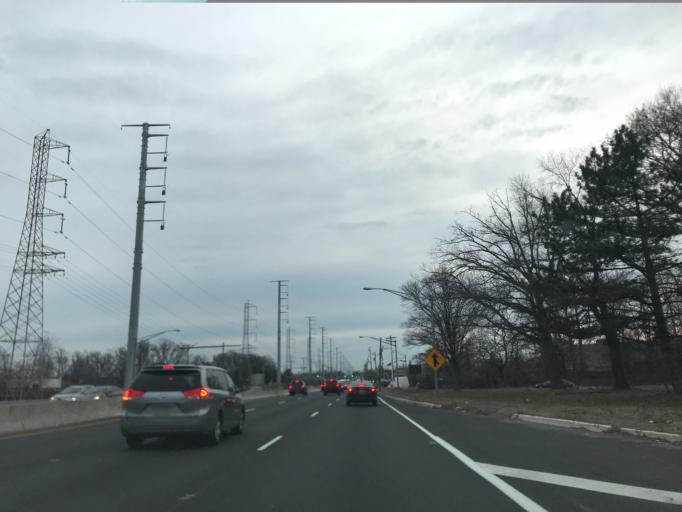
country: US
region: New Jersey
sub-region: Middlesex County
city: Metuchen
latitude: 40.5253
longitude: -74.3588
